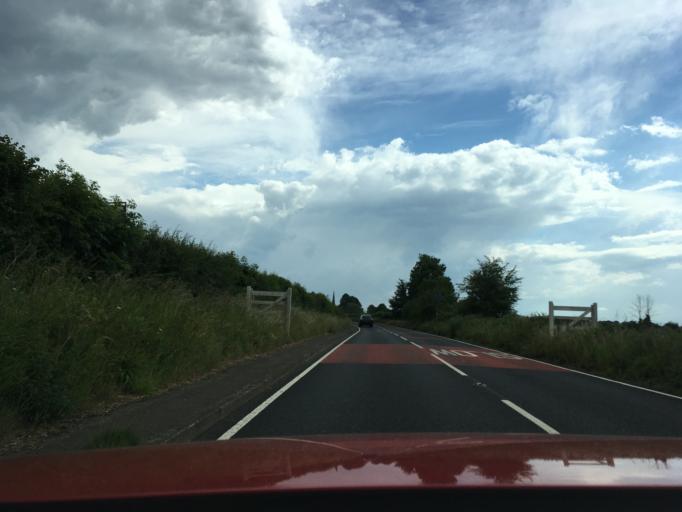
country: GB
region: England
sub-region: Gloucestershire
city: Stonehouse
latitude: 51.7798
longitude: -2.2878
